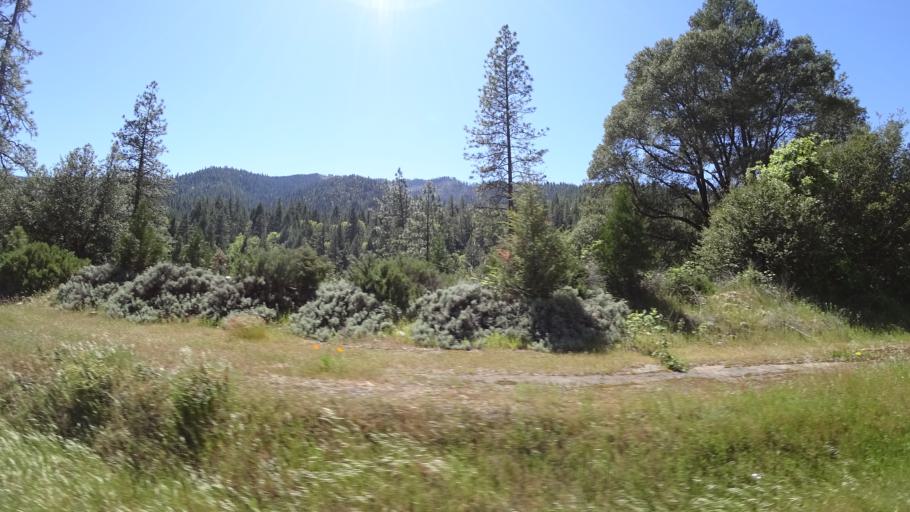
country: US
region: California
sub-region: Trinity County
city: Hayfork
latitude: 40.7428
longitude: -123.2669
